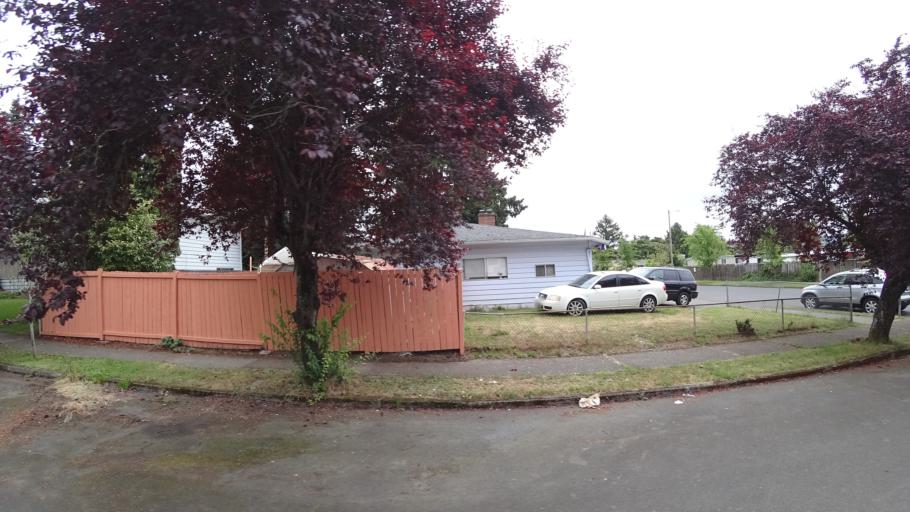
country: US
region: Oregon
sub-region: Multnomah County
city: Lents
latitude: 45.4983
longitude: -122.5504
